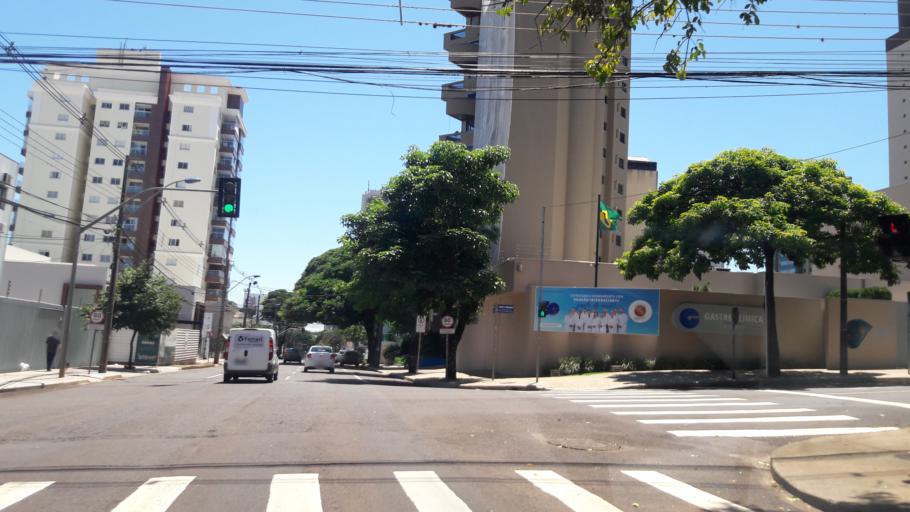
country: BR
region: Parana
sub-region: Cascavel
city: Cascavel
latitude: -24.9514
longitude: -53.4550
